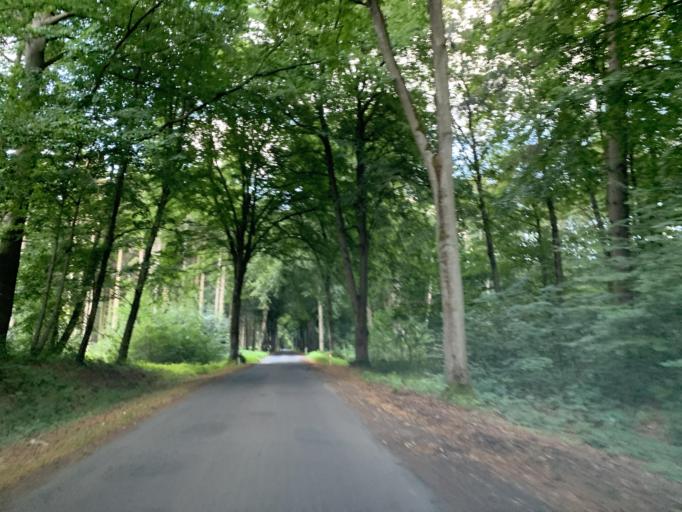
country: DE
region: Mecklenburg-Vorpommern
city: Burg Stargard
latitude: 53.4761
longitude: 13.2832
